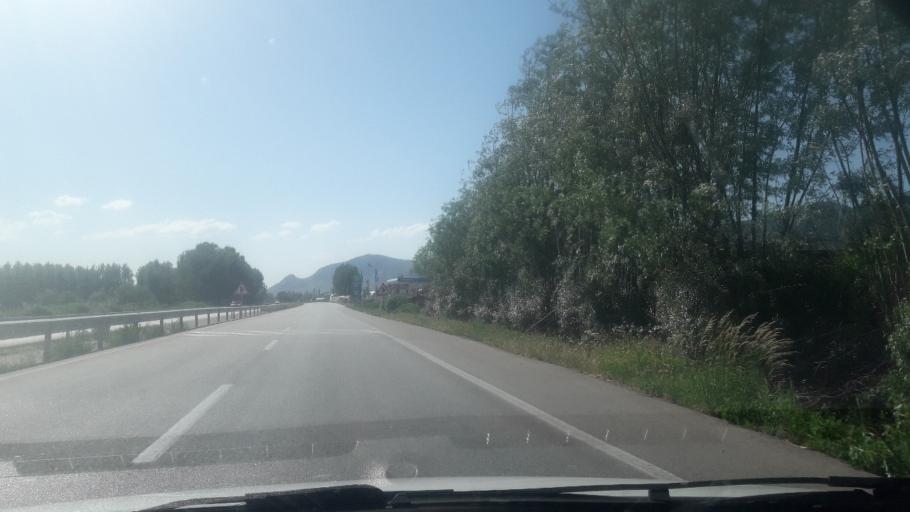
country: TR
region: Tokat
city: Dokmetepe
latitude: 40.3113
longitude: 36.2861
